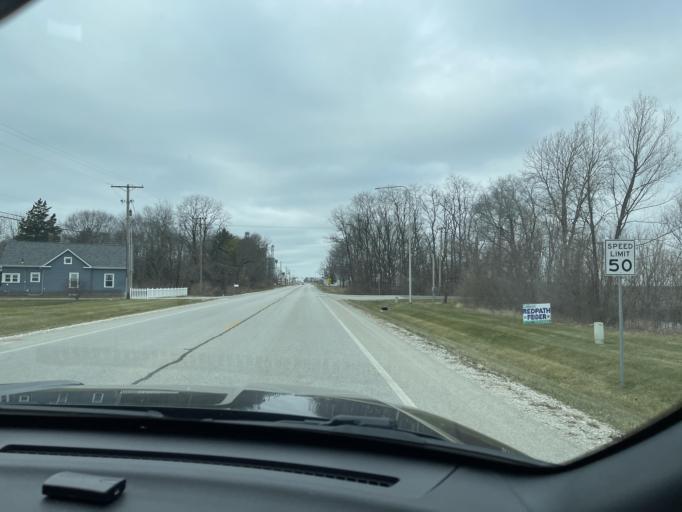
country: US
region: Illinois
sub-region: Sangamon County
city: Leland Grove
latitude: 39.8224
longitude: -89.7341
